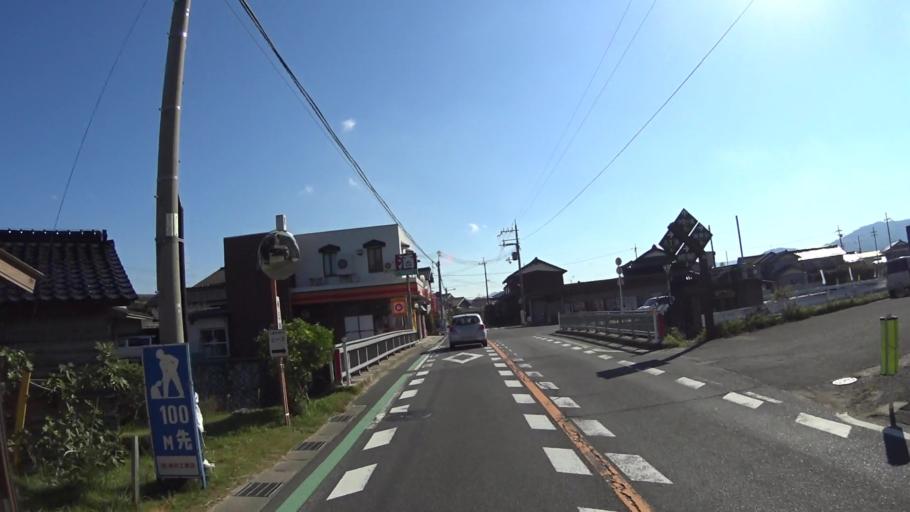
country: JP
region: Kyoto
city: Miyazu
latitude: 35.6907
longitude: 135.0350
